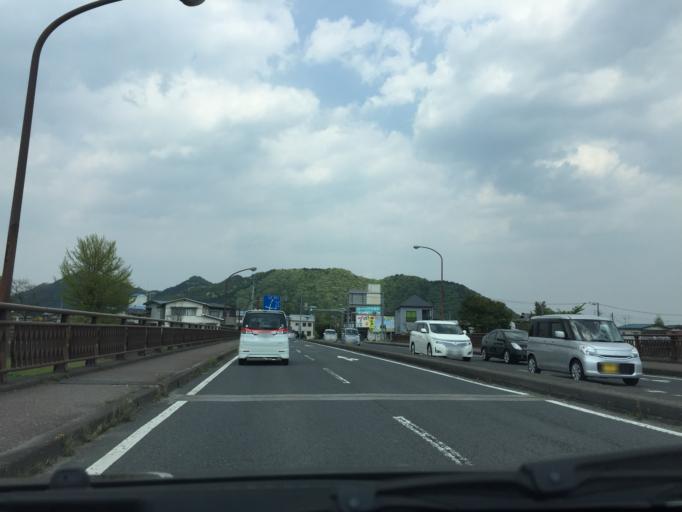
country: JP
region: Tochigi
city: Imaichi
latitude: 36.7319
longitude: 139.6879
